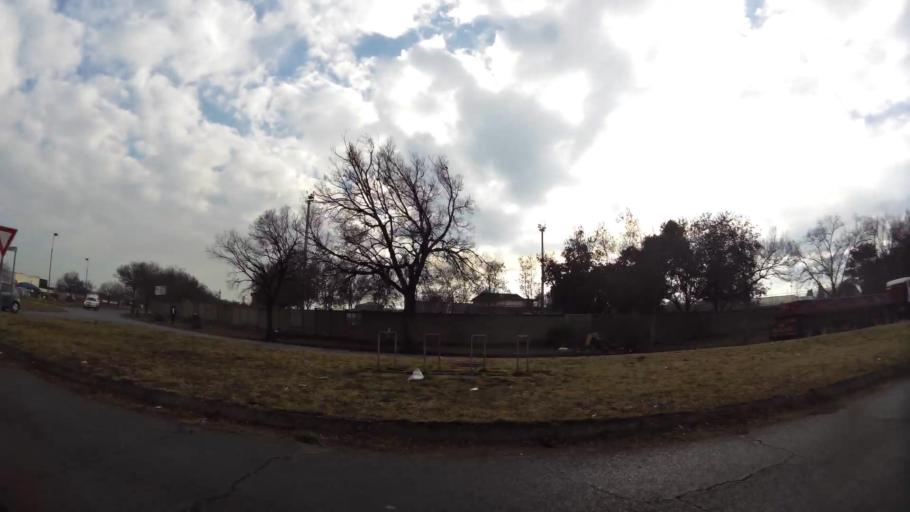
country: ZA
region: Gauteng
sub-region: Sedibeng District Municipality
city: Vanderbijlpark
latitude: -26.6920
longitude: 27.8135
